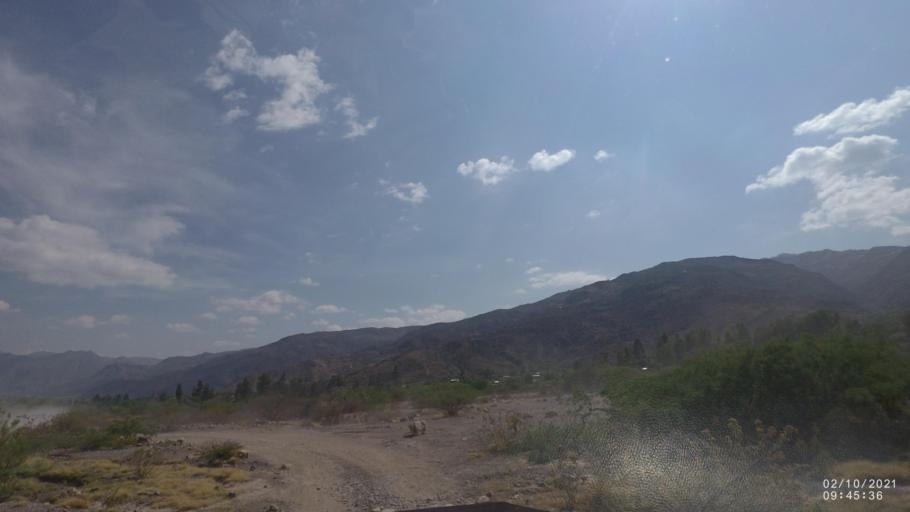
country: BO
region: Cochabamba
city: Irpa Irpa
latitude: -17.8083
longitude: -66.3342
